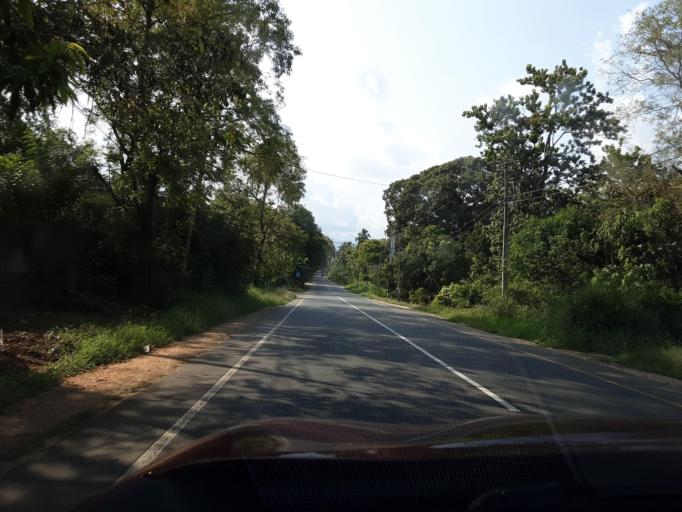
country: LK
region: Uva
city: Haputale
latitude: 6.6146
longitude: 81.1302
